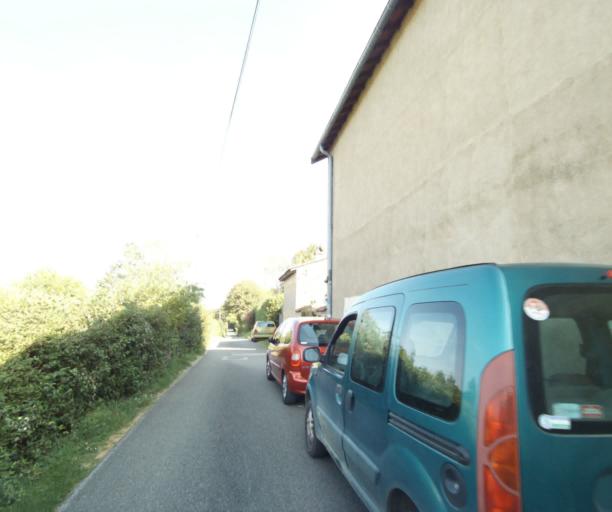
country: FR
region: Bourgogne
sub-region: Departement de Saone-et-Loire
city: Tournus
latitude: 46.5606
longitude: 4.8927
